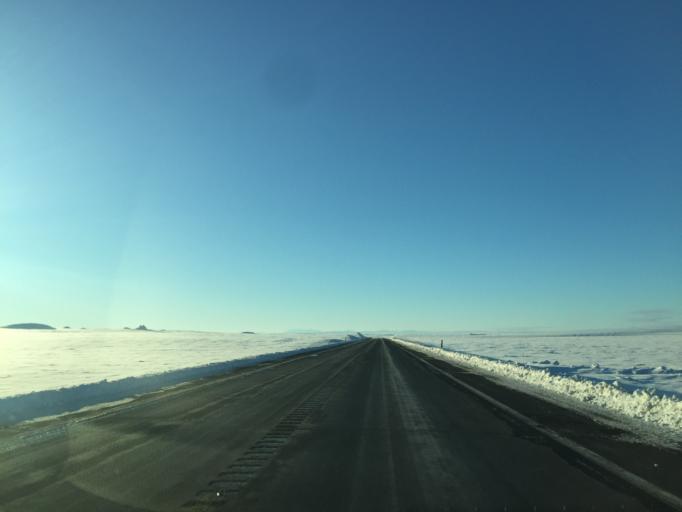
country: US
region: Washington
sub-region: Grant County
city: Soap Lake
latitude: 47.6199
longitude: -119.4407
